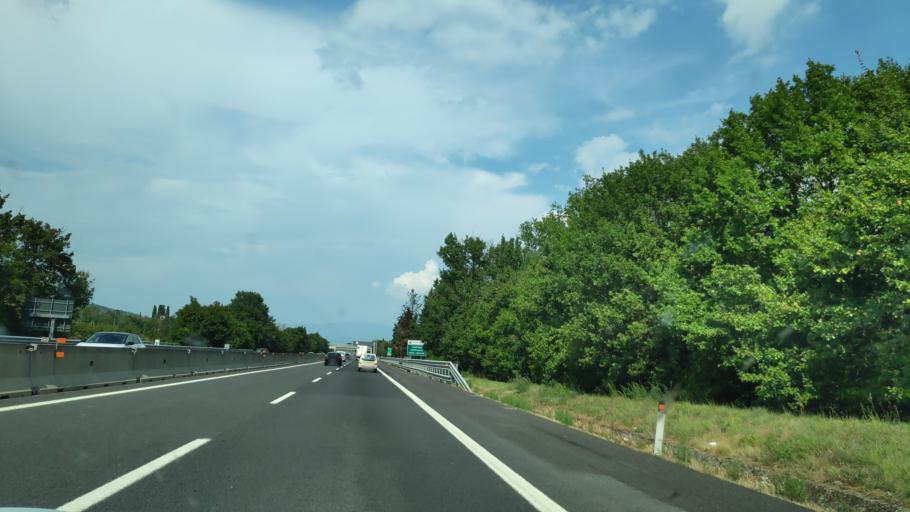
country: IT
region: Tuscany
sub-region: Province of Arezzo
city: Viciomaggio
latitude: 43.4195
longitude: 11.7727
